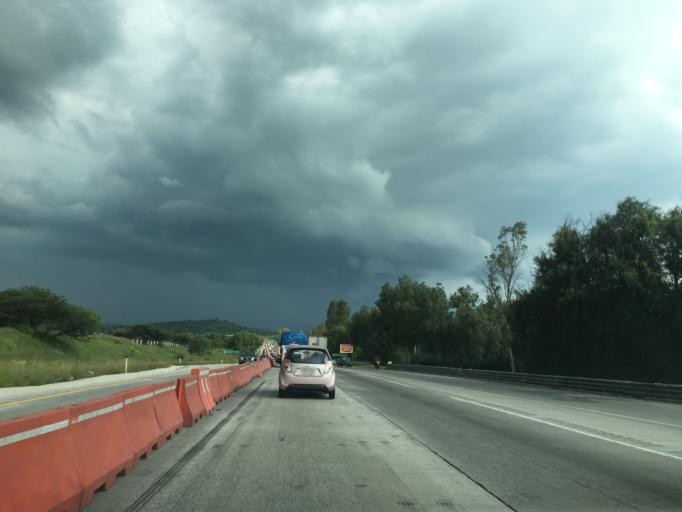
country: MX
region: Hidalgo
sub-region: Tepeji del Rio de Ocampo
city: Santiago Tlapanaloya
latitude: 19.8785
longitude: -99.3422
